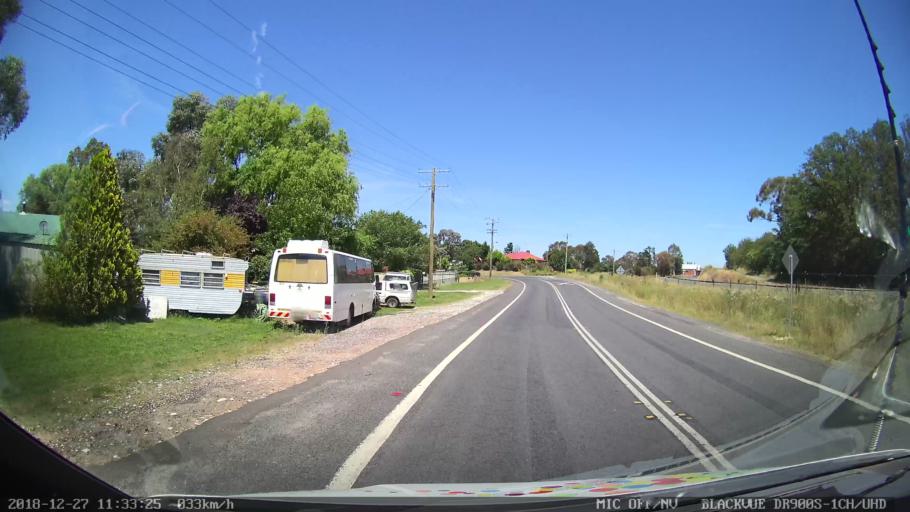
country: AU
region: New South Wales
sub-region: Bathurst Regional
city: Perthville
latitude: -33.5134
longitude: 149.5251
